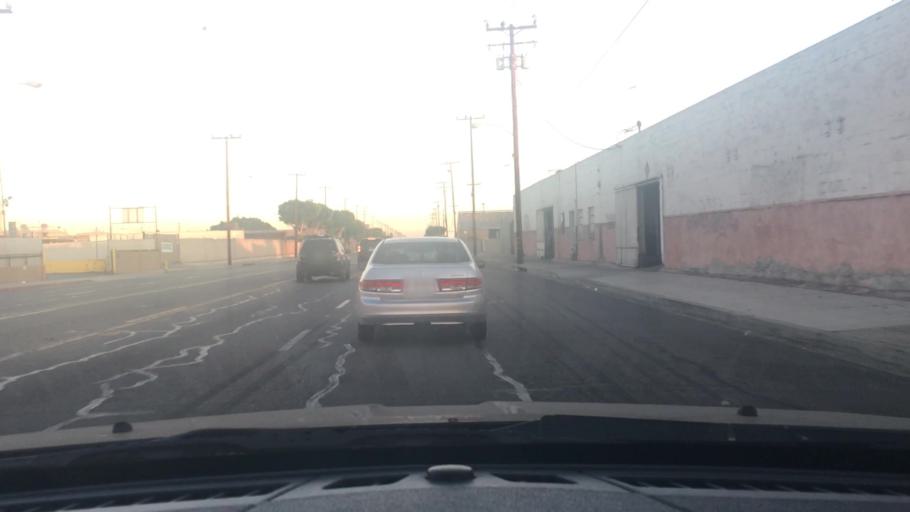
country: US
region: California
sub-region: Los Angeles County
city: Maywood
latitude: 34.0059
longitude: -118.1980
